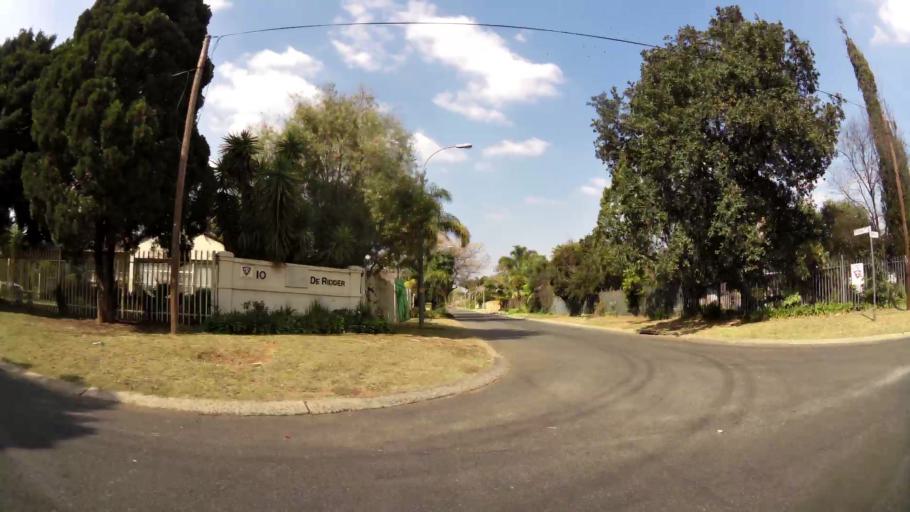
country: ZA
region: Gauteng
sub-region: City of Johannesburg Metropolitan Municipality
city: Modderfontein
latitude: -26.0799
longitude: 28.2375
